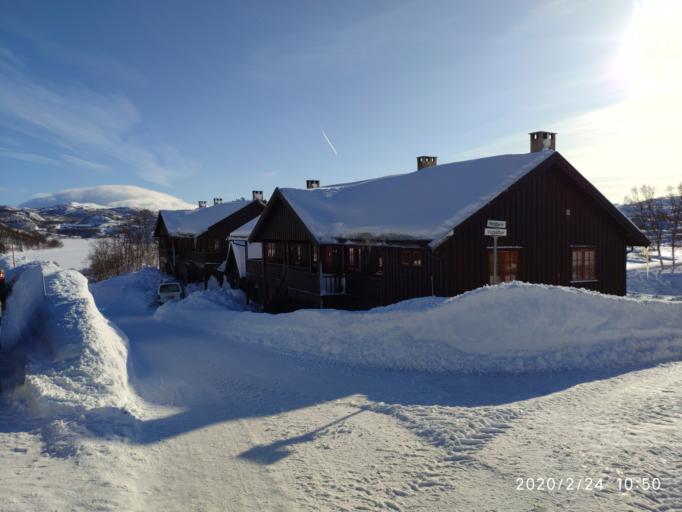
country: NO
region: Aust-Agder
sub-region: Bykle
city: Hovden
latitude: 59.7696
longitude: 7.3895
